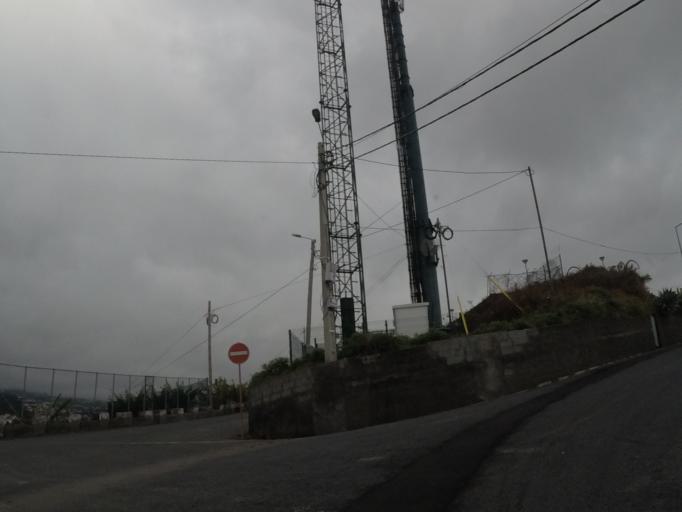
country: PT
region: Madeira
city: Camara de Lobos
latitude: 32.6521
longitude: -16.9743
